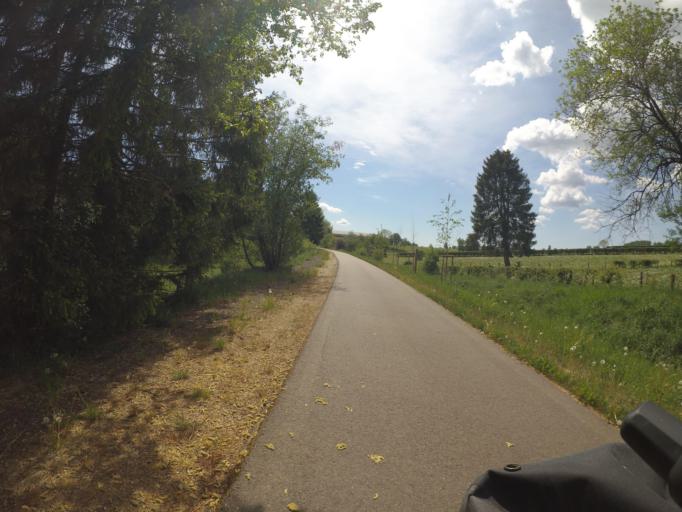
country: BE
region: Wallonia
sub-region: Province de Liege
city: Bullange
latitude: 50.3901
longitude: 6.2735
